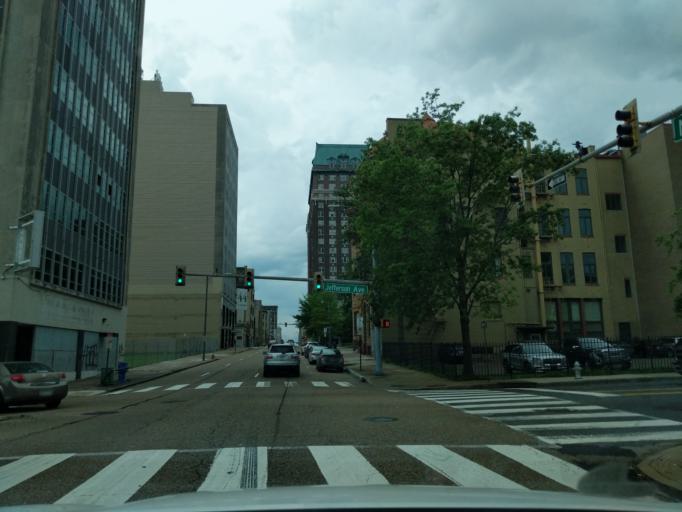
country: US
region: Tennessee
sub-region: Shelby County
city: Memphis
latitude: 35.1471
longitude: -90.0507
